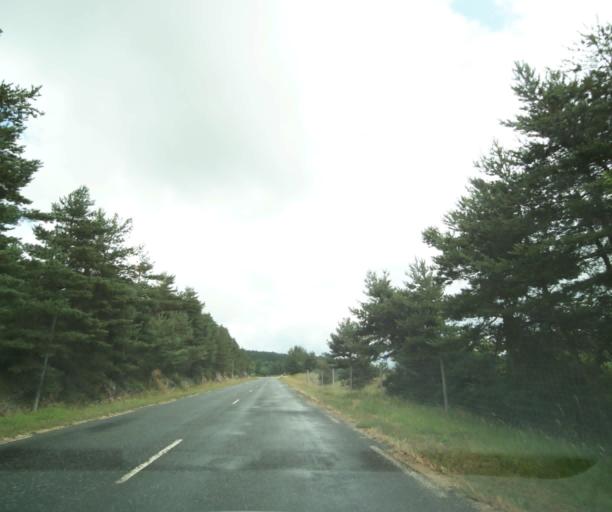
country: FR
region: Languedoc-Roussillon
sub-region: Departement de la Lozere
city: La Canourgue
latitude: 44.3951
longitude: 3.1281
